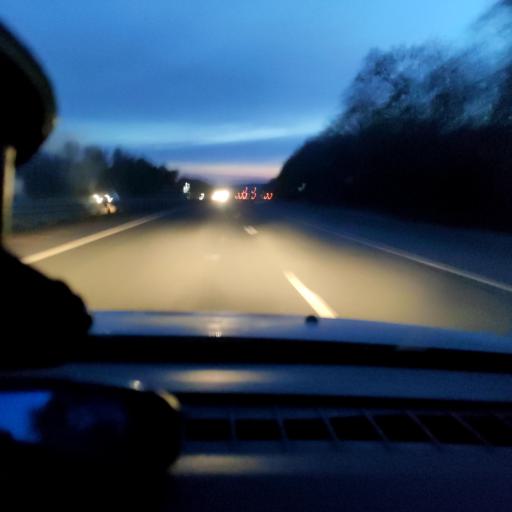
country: RU
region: Samara
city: Novokuybyshevsk
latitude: 53.0514
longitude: 50.0109
